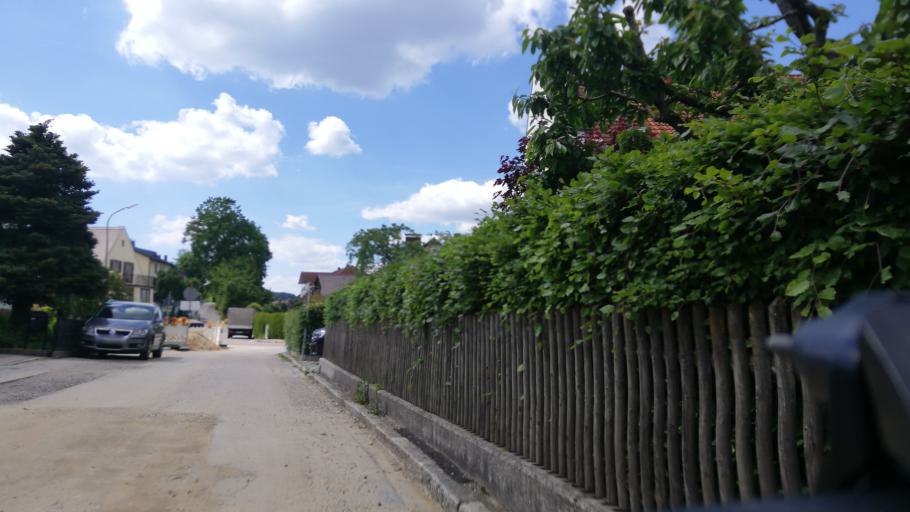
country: DE
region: Bavaria
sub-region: Upper Bavaria
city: Pfaffenhofen an der Ilm
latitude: 48.5333
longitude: 11.4939
